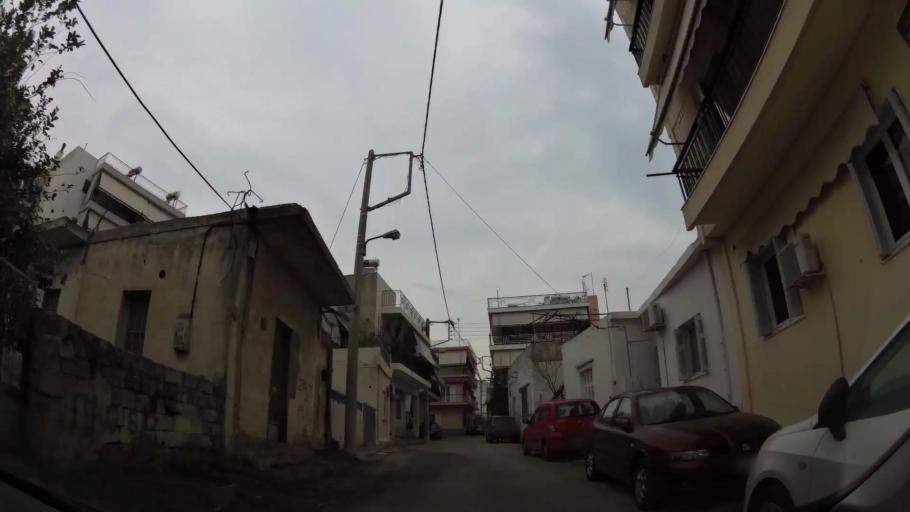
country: GR
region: Attica
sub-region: Nomarchia Athinas
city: Ilion
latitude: 38.0233
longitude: 23.7046
